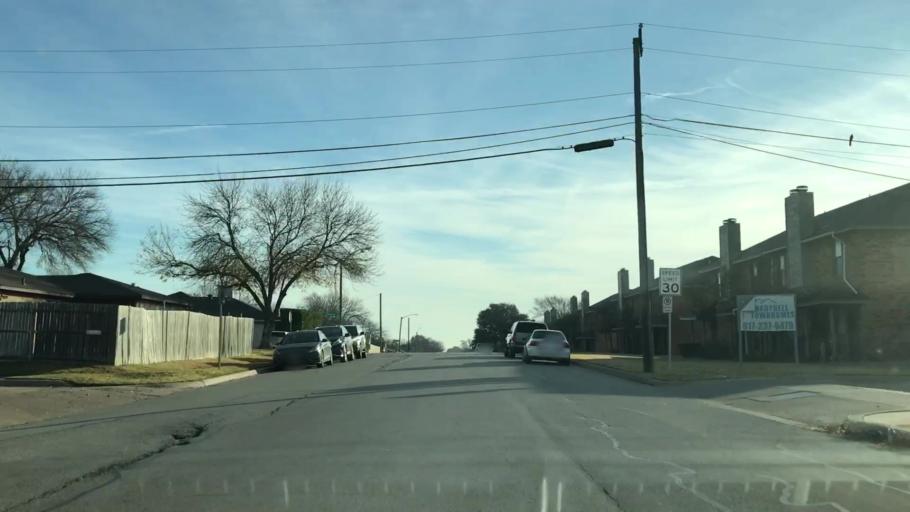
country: US
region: Texas
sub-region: Tarrant County
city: Sansom Park
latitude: 32.8220
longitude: -97.4191
